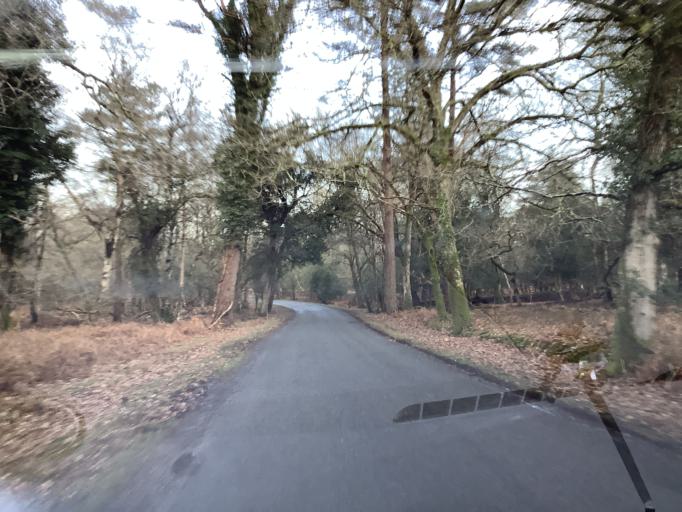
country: GB
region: England
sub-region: Hampshire
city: Lyndhurst
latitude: 50.8691
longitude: -1.6411
